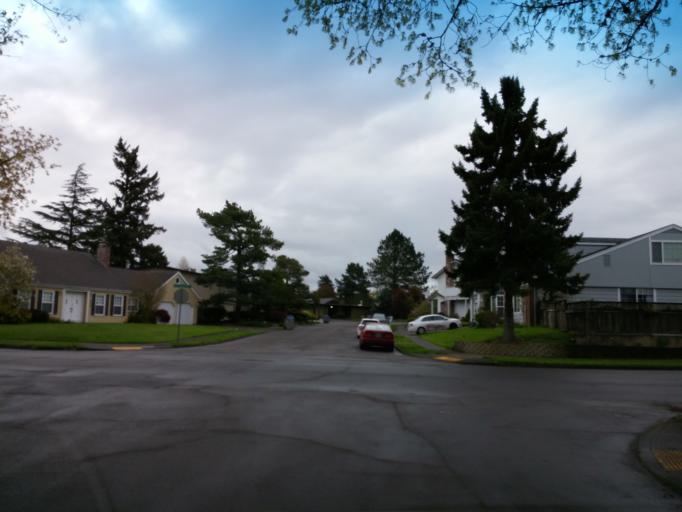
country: US
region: Oregon
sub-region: Washington County
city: Oak Hills
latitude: 45.5399
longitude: -122.8393
